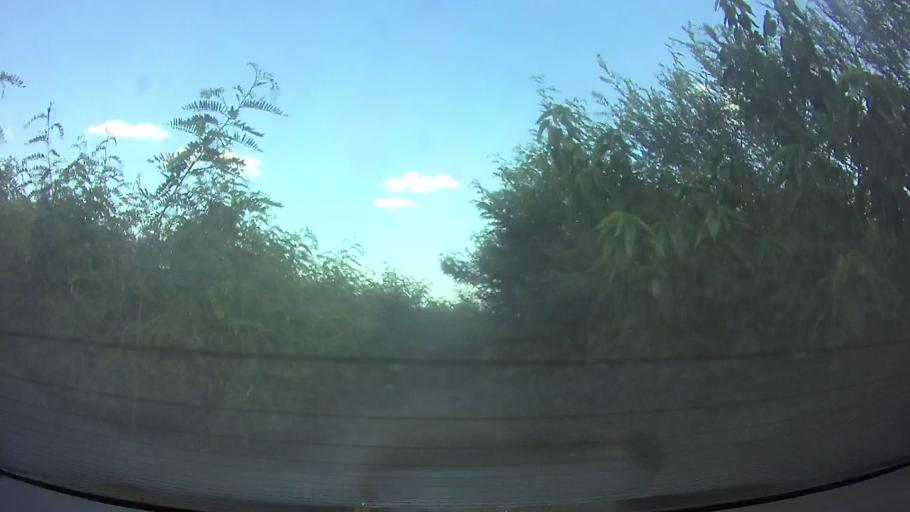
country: PY
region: Cordillera
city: Arroyos y Esteros
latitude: -24.9706
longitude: -57.1915
